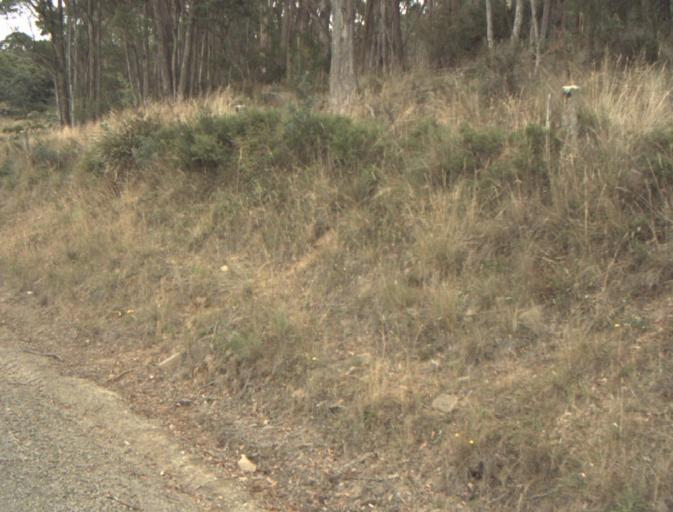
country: AU
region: Tasmania
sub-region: Northern Midlands
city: Evandale
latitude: -41.4826
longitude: 147.4418
